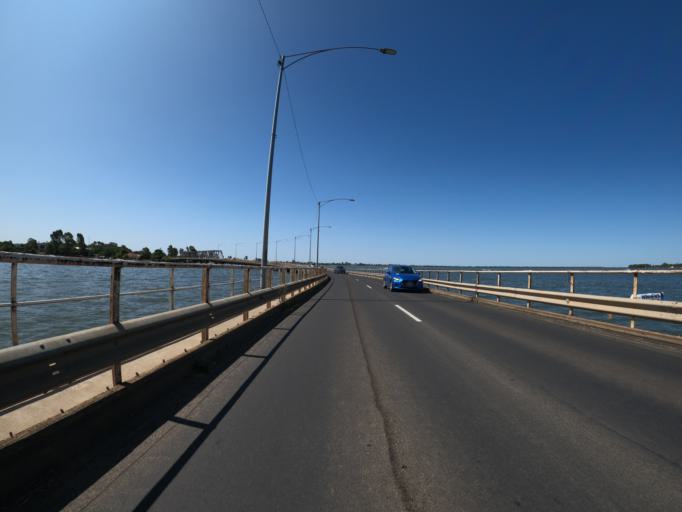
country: AU
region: Victoria
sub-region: Moira
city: Yarrawonga
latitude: -36.0064
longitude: 146.0050
